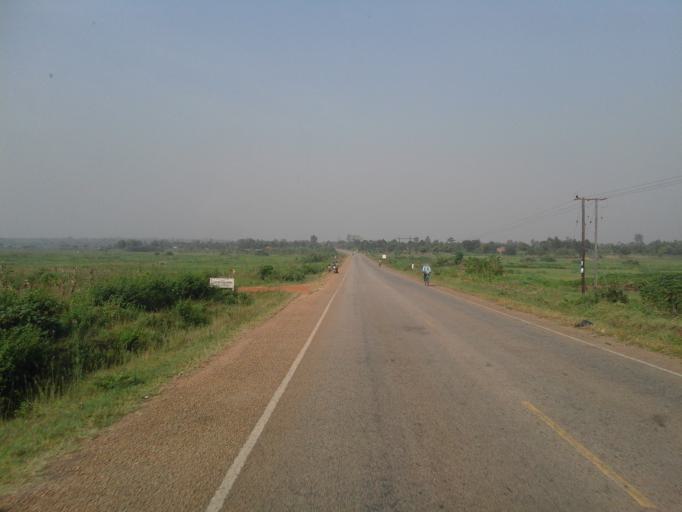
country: UG
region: Eastern Region
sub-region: Mbale District
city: Mbale
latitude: 1.0546
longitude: 34.0609
